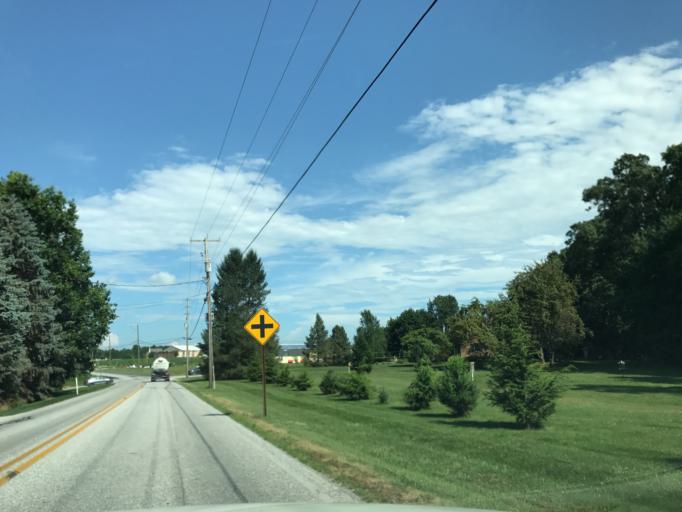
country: US
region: Pennsylvania
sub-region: York County
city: Pennville
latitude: 39.7608
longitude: -76.9875
